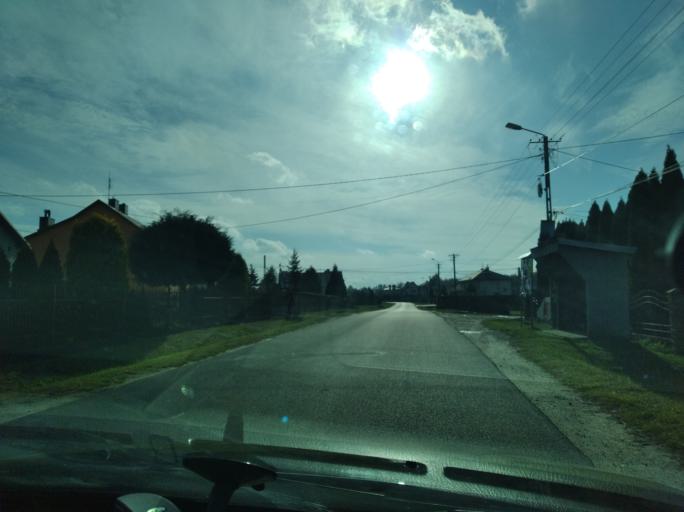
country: PL
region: Subcarpathian Voivodeship
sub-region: Powiat ropczycko-sedziszowski
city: Sedziszow Malopolski
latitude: 50.1067
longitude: 21.7334
